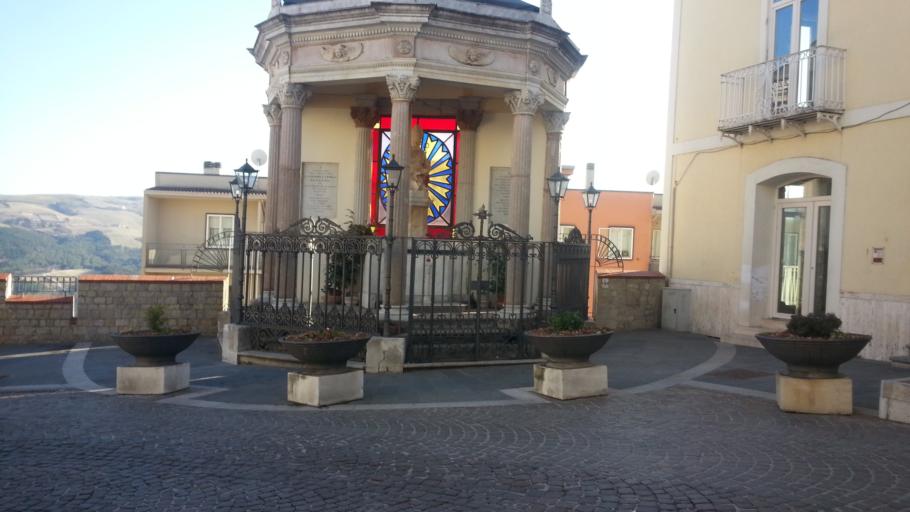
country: IT
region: Basilicate
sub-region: Provincia di Potenza
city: Potenza
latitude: 40.6386
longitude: 15.8056
